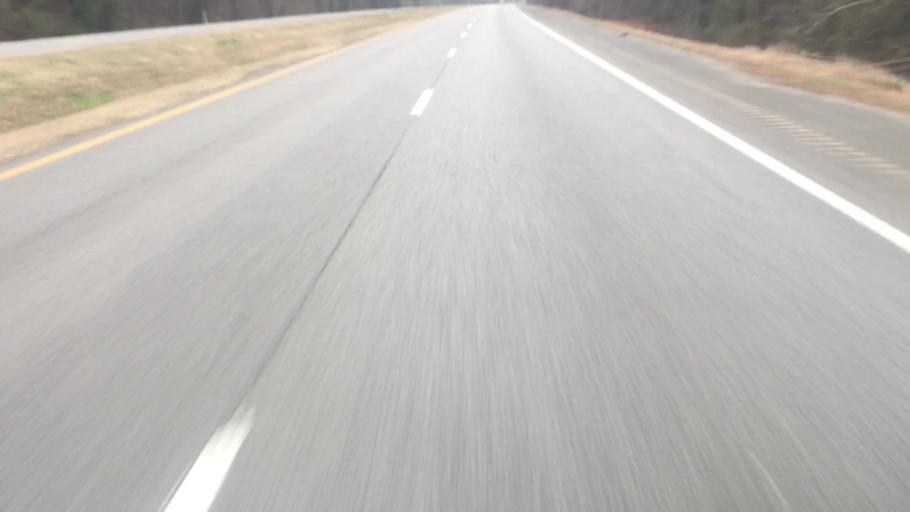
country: US
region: Alabama
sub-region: Jefferson County
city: Graysville
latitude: 33.6718
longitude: -86.9713
